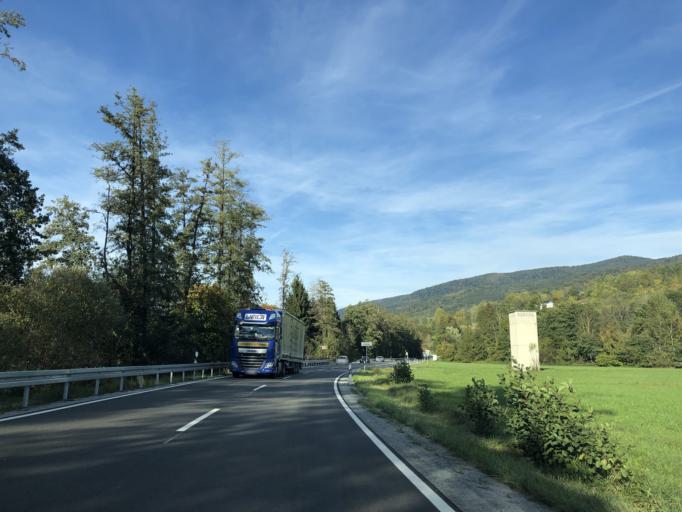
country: DE
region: Bavaria
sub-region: Lower Bavaria
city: Grafling
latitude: 48.8781
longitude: 12.9617
